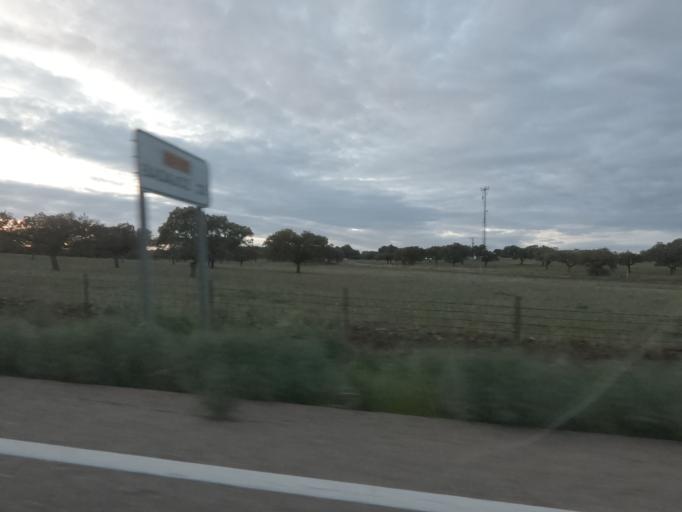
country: ES
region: Extremadura
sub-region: Provincia de Badajoz
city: Villar del Rey
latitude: 39.0320
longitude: -6.8282
